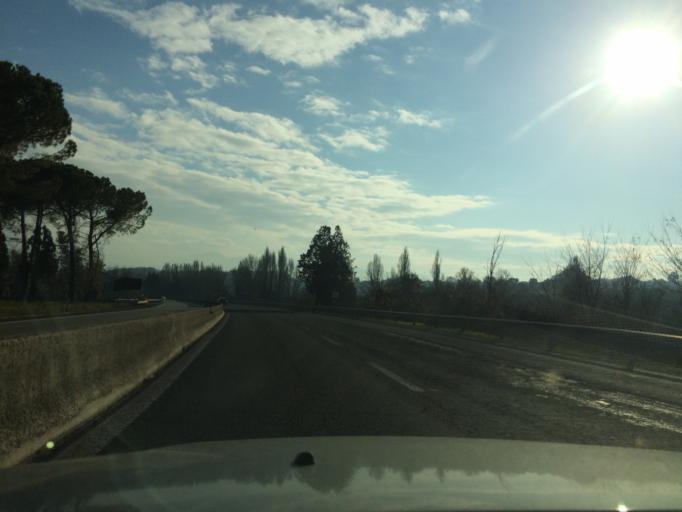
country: IT
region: Umbria
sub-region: Provincia di Terni
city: San Gemini
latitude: 42.5941
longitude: 12.5633
